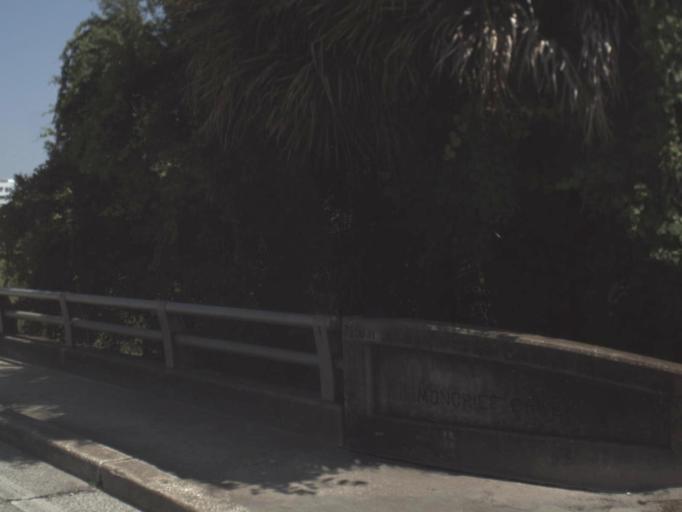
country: US
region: Florida
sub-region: Duval County
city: Jacksonville
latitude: 30.3810
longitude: -81.6710
